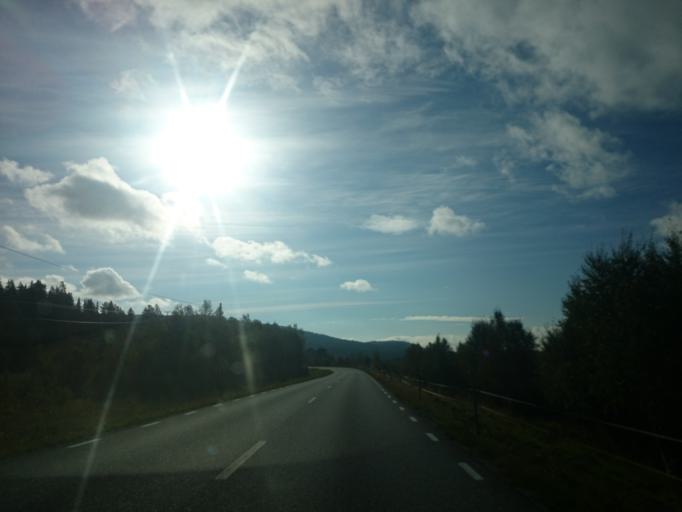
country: SE
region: Jaemtland
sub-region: Are Kommun
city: Are
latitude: 62.6021
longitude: 12.5185
